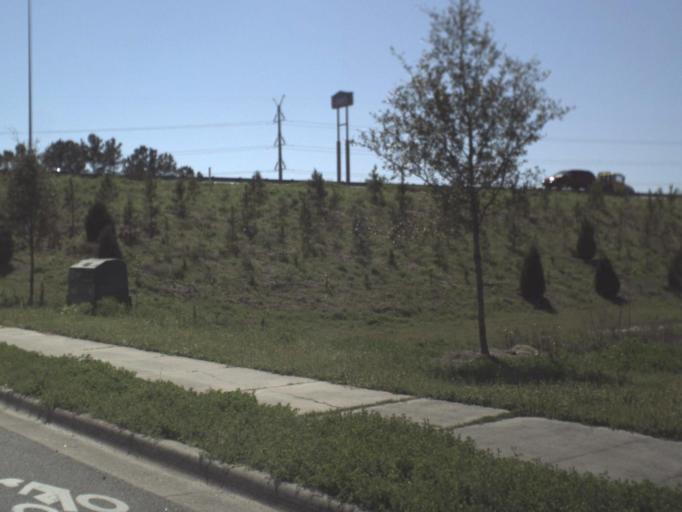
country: US
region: Florida
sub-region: Gadsden County
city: Midway
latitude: 30.4804
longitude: -84.3634
